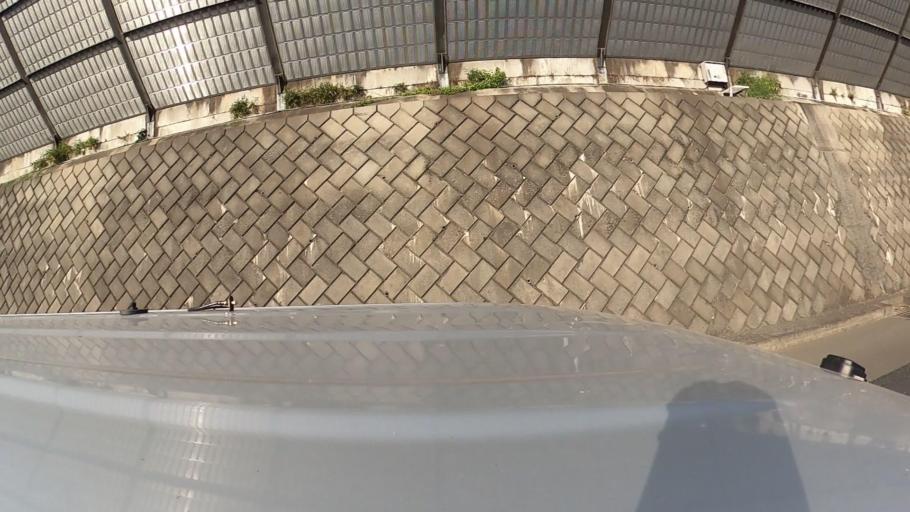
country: JP
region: Saitama
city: Shiki
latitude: 35.7937
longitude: 139.5441
